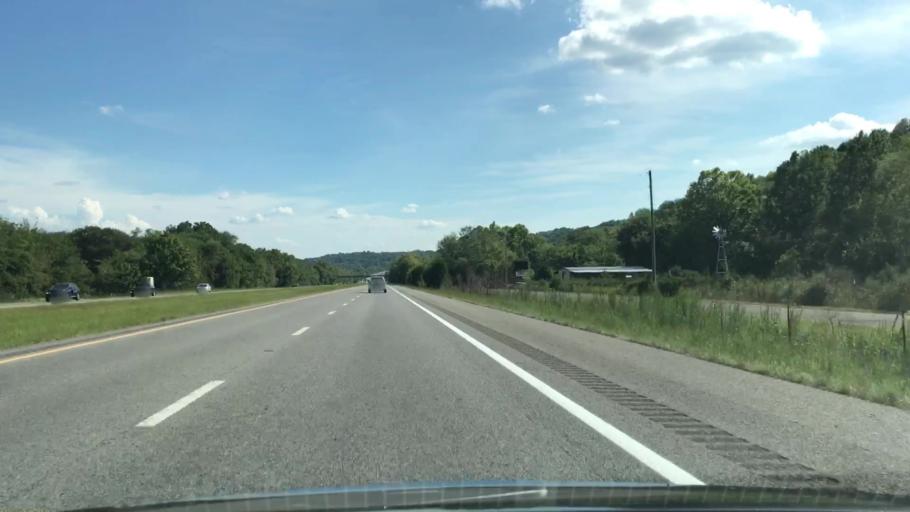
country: US
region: Alabama
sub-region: Limestone County
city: Ardmore
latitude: 35.1451
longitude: -86.8789
